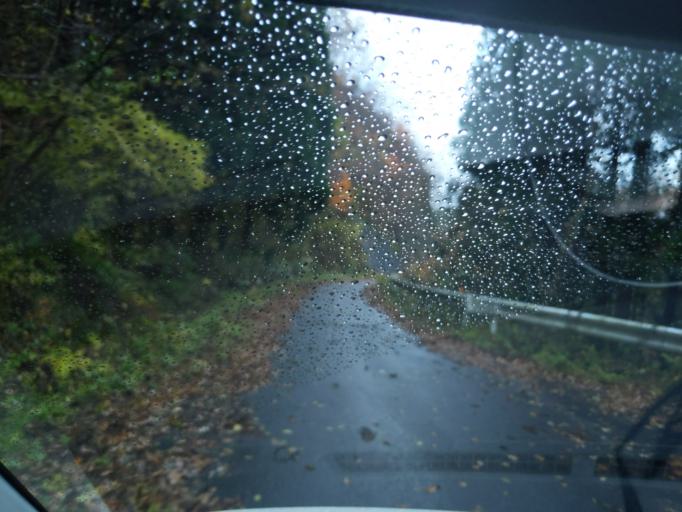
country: JP
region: Iwate
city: Mizusawa
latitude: 39.0973
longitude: 140.9381
